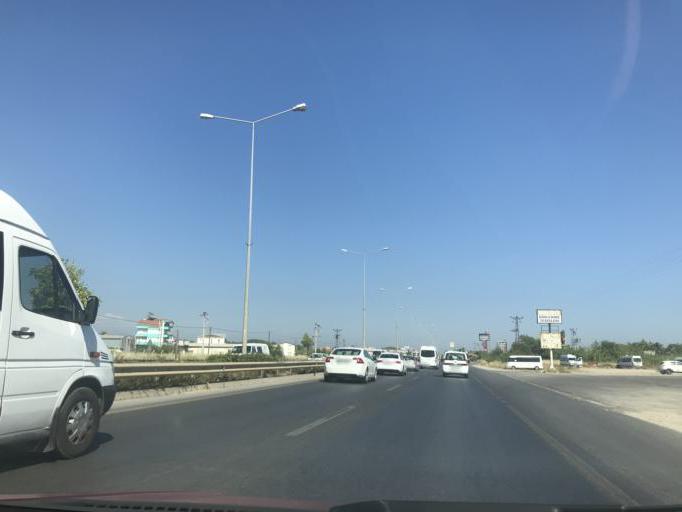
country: TR
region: Antalya
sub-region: Manavgat
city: Side
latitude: 36.8142
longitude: 31.3686
